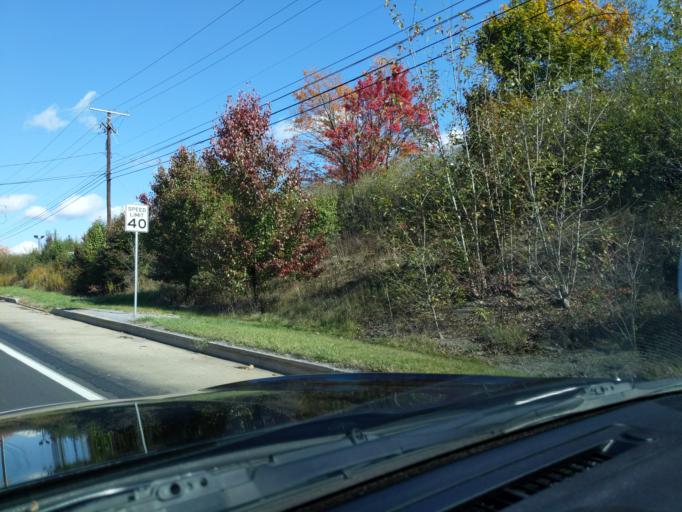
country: US
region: Pennsylvania
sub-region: Blair County
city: Lakemont
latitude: 40.4525
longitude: -78.4096
